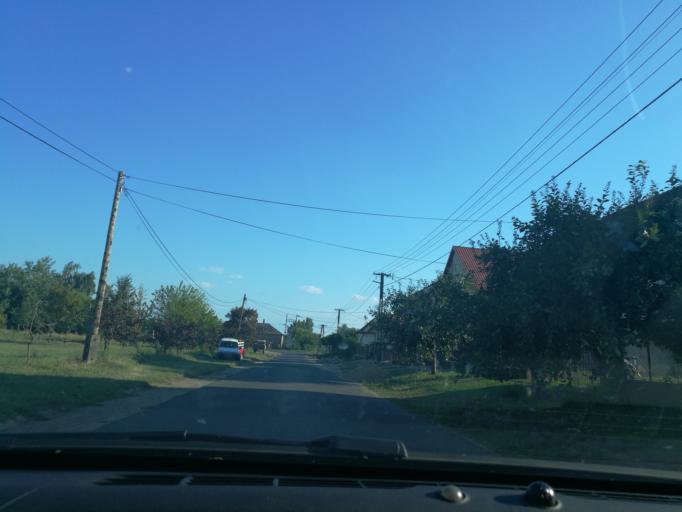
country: HU
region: Szabolcs-Szatmar-Bereg
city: Tiszabercel
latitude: 48.1669
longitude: 21.5643
